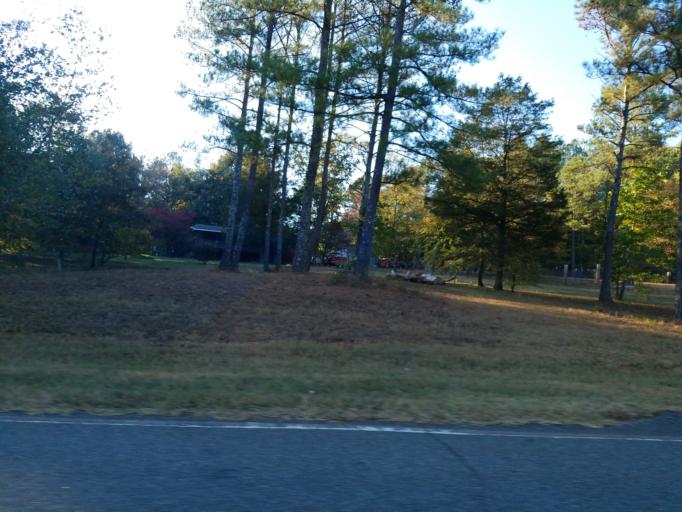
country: US
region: Georgia
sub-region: Bartow County
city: Adairsville
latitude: 34.2821
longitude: -84.9462
